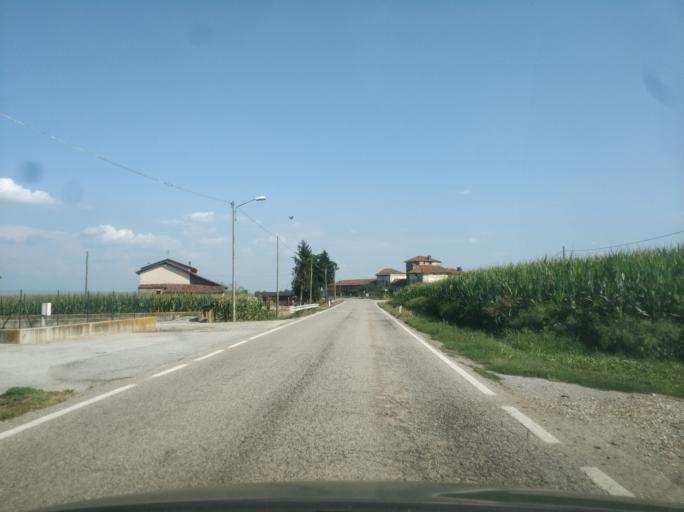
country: IT
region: Piedmont
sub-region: Provincia di Cuneo
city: Centallo
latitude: 44.5343
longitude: 7.6269
